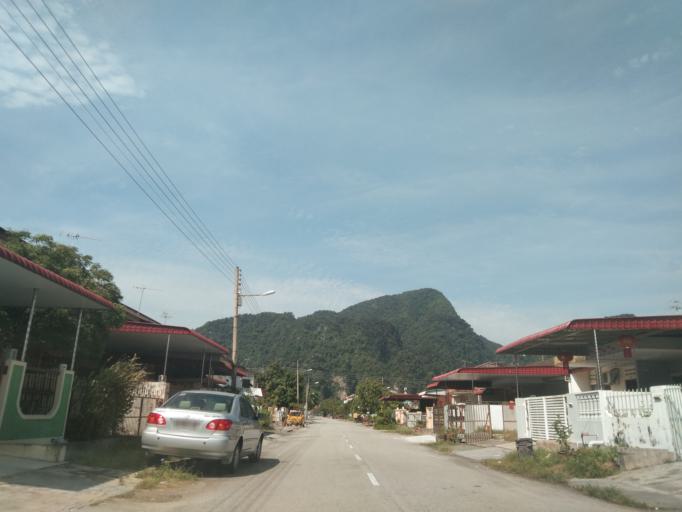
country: MY
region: Perak
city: Ipoh
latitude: 4.5681
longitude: 101.1288
